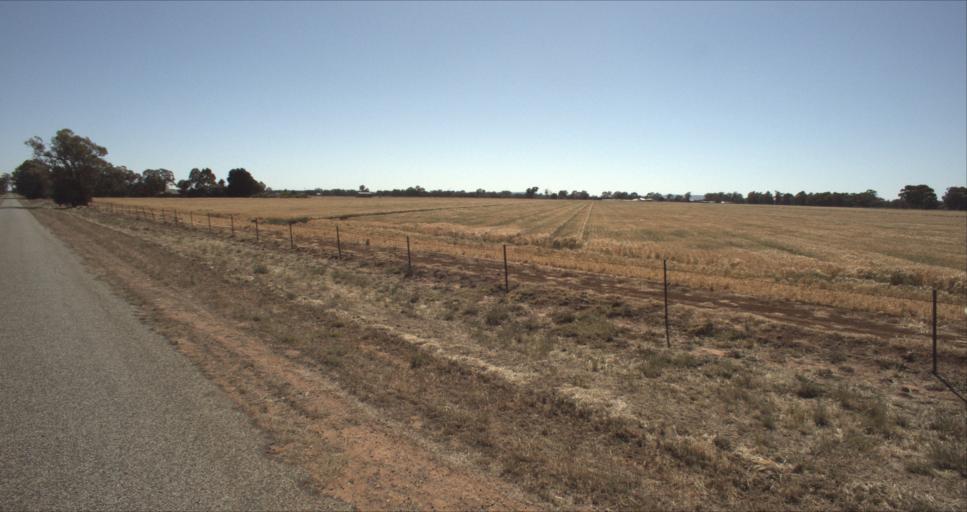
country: AU
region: New South Wales
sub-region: Leeton
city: Leeton
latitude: -34.5478
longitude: 146.3152
